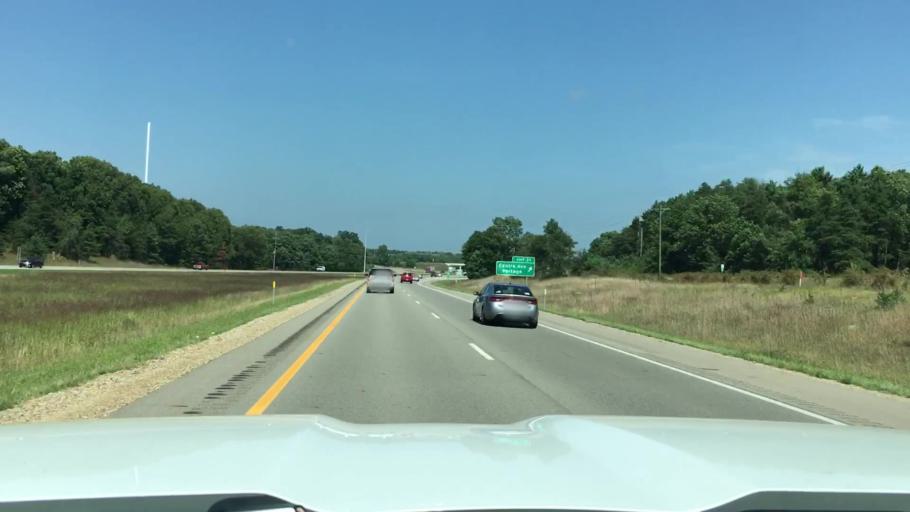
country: US
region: Michigan
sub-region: Kalamazoo County
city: Portage
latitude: 42.1926
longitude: -85.6463
